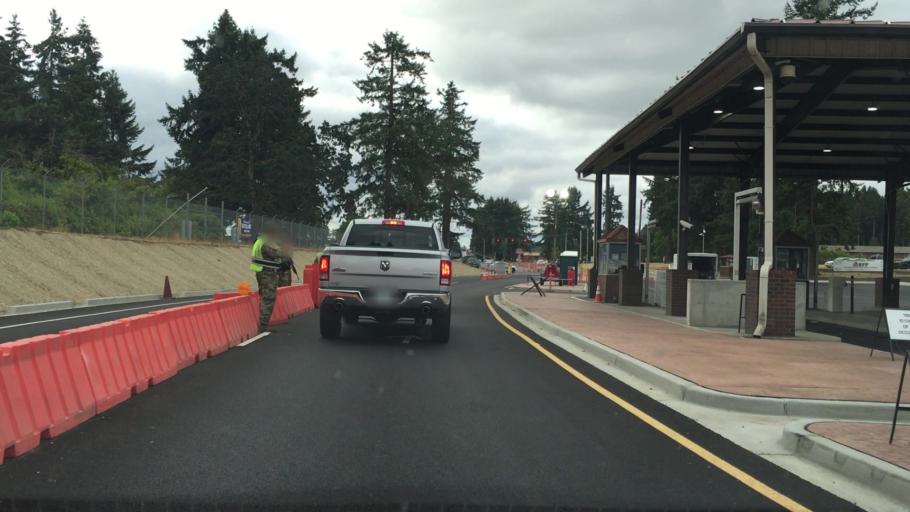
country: US
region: Washington
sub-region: Pierce County
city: Fort Lewis
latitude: 47.1008
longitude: -122.5864
